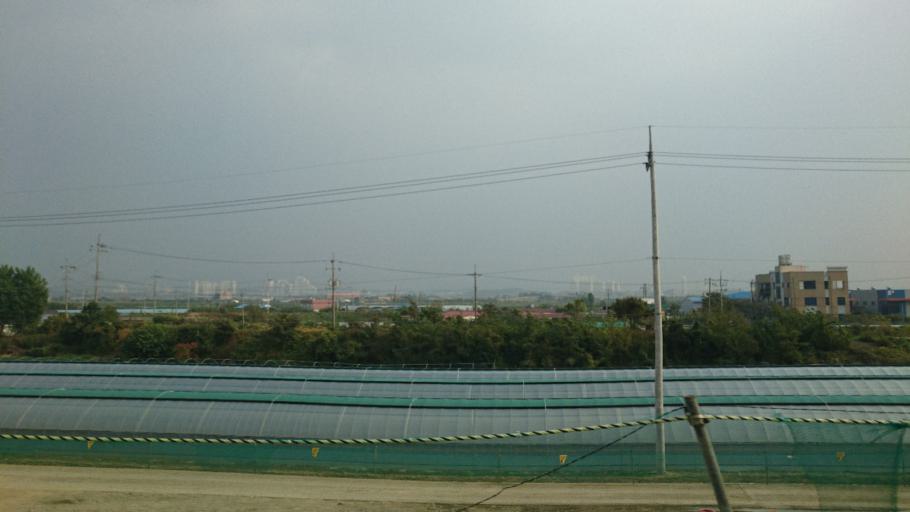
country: KR
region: Gyeongsangbuk-do
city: Hayang
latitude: 35.8851
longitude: 128.7766
